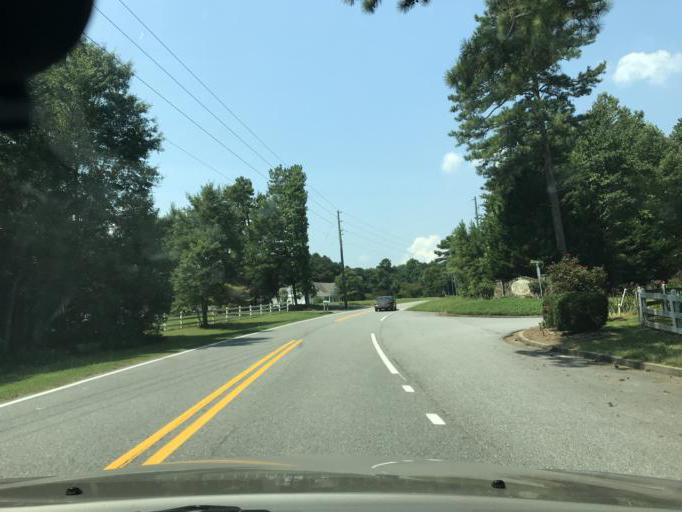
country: US
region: Georgia
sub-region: Forsyth County
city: Cumming
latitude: 34.3095
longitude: -84.0860
